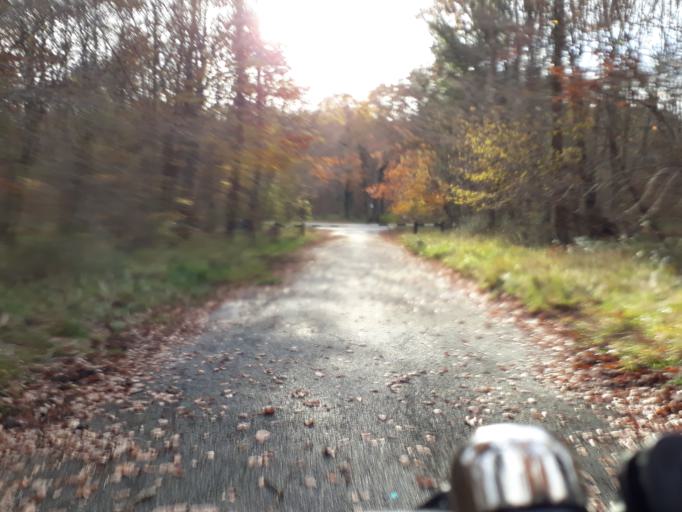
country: FR
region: Ile-de-France
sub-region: Departement de Seine-et-Marne
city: Bois-le-Roi
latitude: 48.4612
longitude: 2.6836
